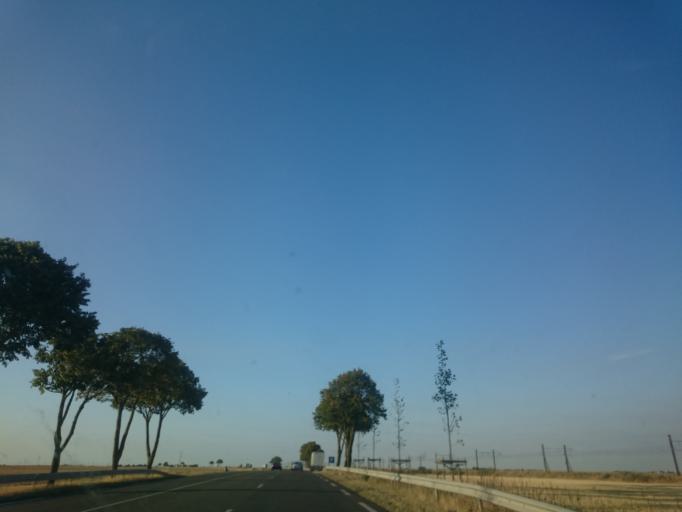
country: FR
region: Centre
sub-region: Departement d'Eure-et-Loir
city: Toury
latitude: 48.2105
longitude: 1.9473
